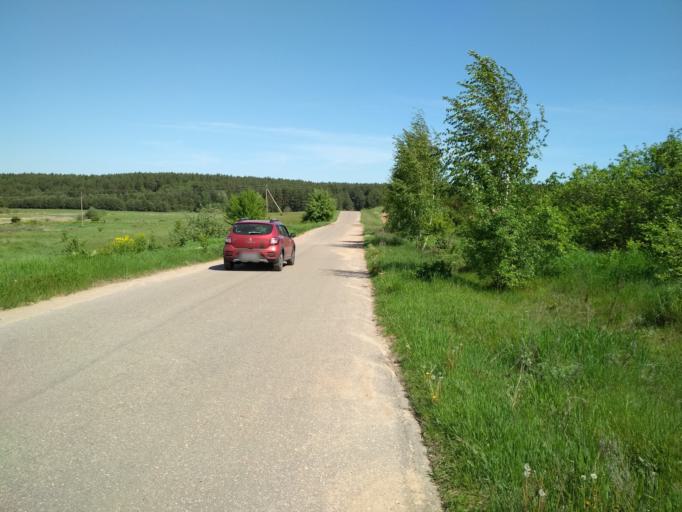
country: BY
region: Grodnenskaya
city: Mir
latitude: 53.3861
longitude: 26.3623
